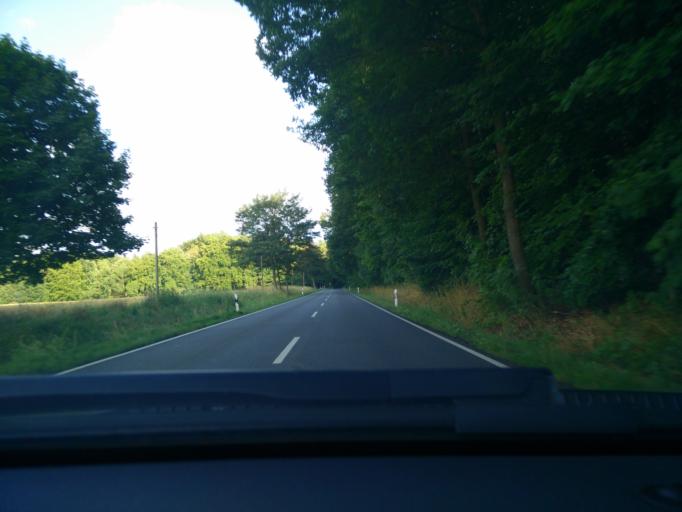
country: DE
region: Saxony
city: Geithain
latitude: 51.0830
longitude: 12.7180
